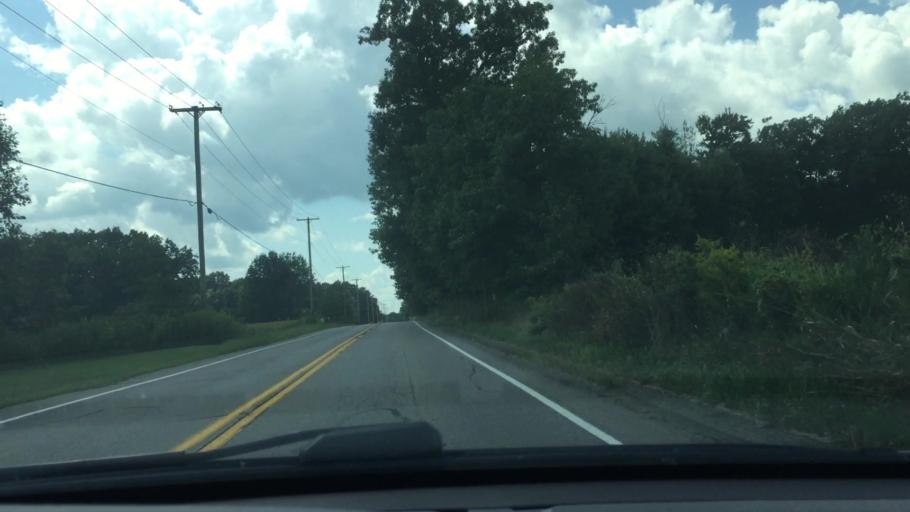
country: US
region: Pennsylvania
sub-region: Mercer County
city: Mercer
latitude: 41.1303
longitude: -80.2259
